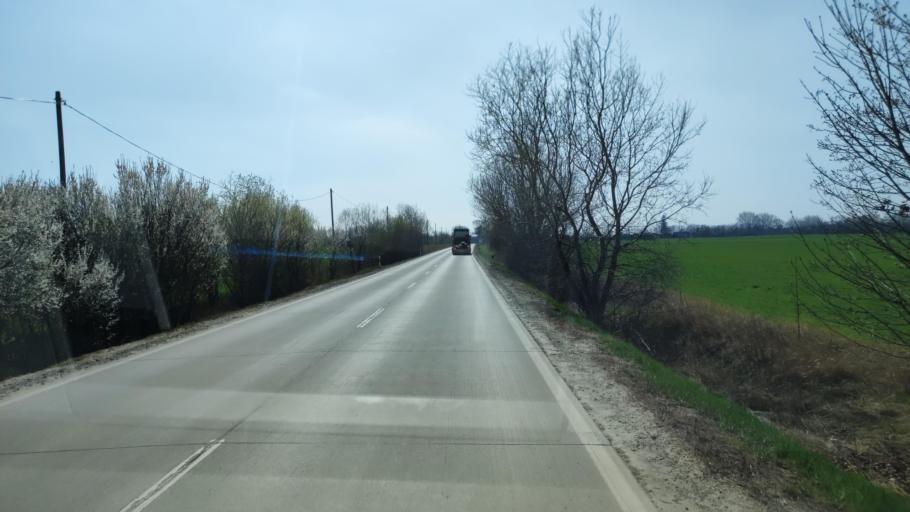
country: HU
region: Pest
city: Kiskunlachaza
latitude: 47.1852
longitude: 19.0519
